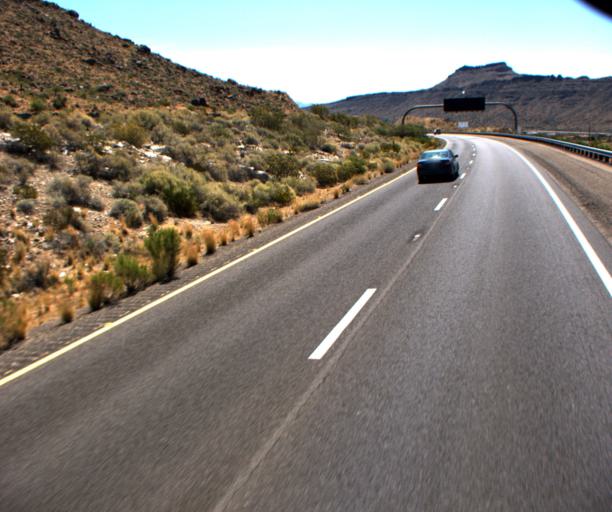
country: US
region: Arizona
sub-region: Mohave County
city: Golden Valley
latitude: 35.2292
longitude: -114.1358
